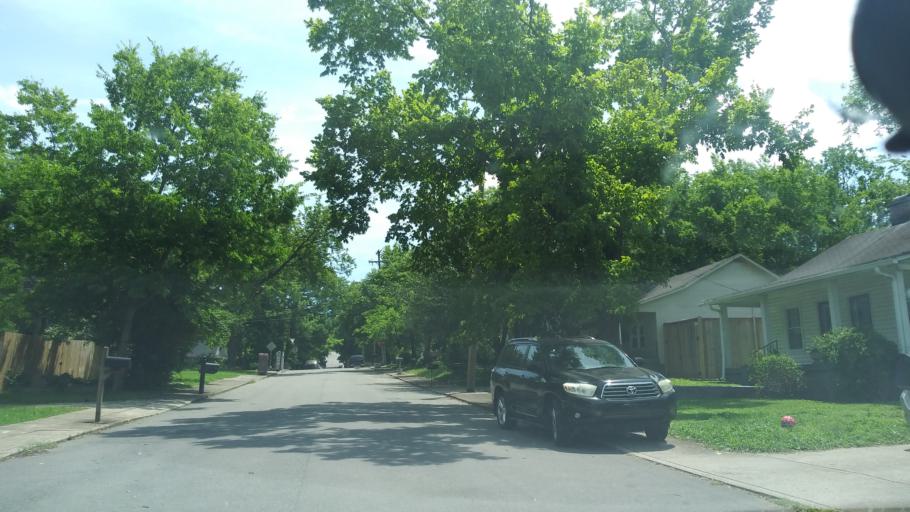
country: US
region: Tennessee
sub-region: Davidson County
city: Nashville
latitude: 36.1493
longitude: -86.8346
